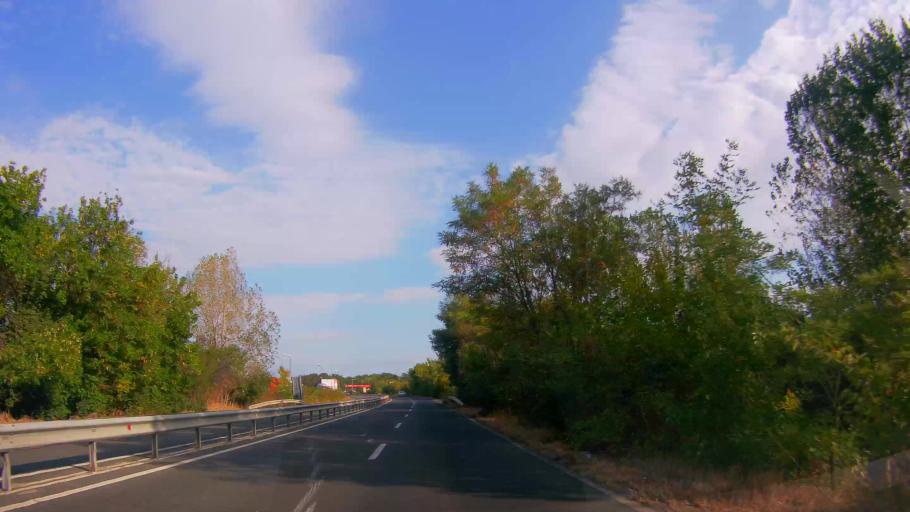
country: BG
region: Burgas
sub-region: Obshtina Sozopol
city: Chernomorets
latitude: 42.4359
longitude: 27.6372
